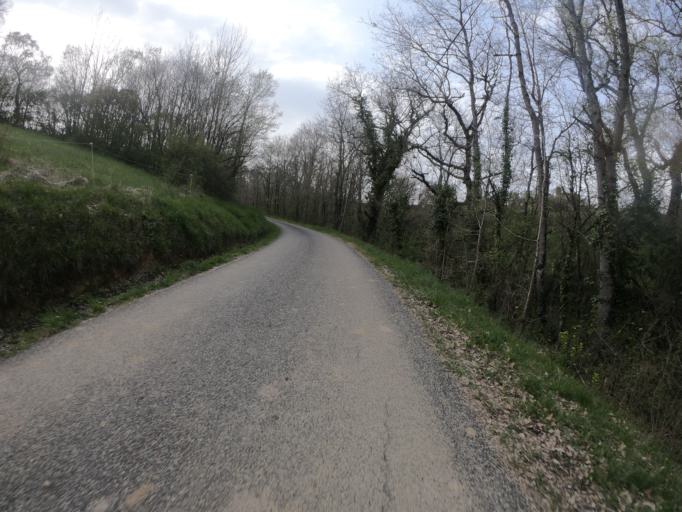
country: FR
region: Languedoc-Roussillon
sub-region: Departement de l'Aude
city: Belpech
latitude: 43.1290
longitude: 1.7490
